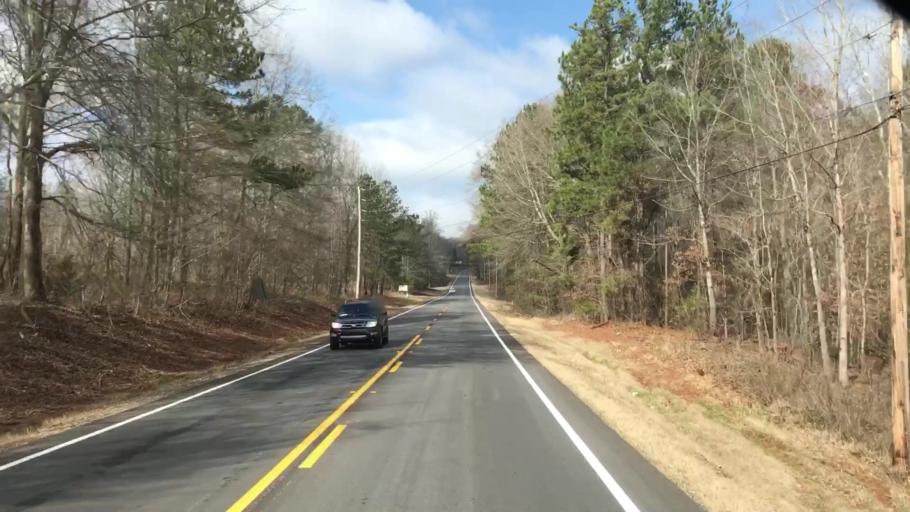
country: US
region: Georgia
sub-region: Jackson County
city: Braselton
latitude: 34.1358
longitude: -83.8338
